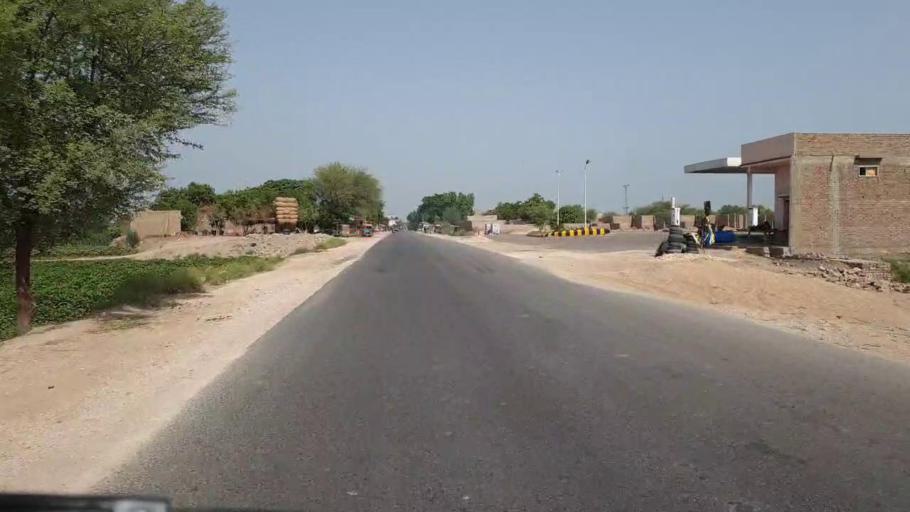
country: PK
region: Sindh
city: Sakrand
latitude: 26.2477
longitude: 68.2147
